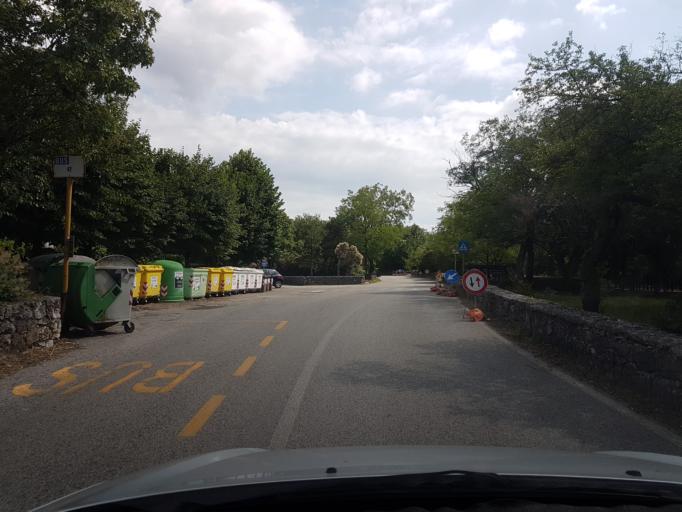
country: IT
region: Friuli Venezia Giulia
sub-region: Provincia di Trieste
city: Villa Opicina
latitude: 45.7128
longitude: 13.7715
